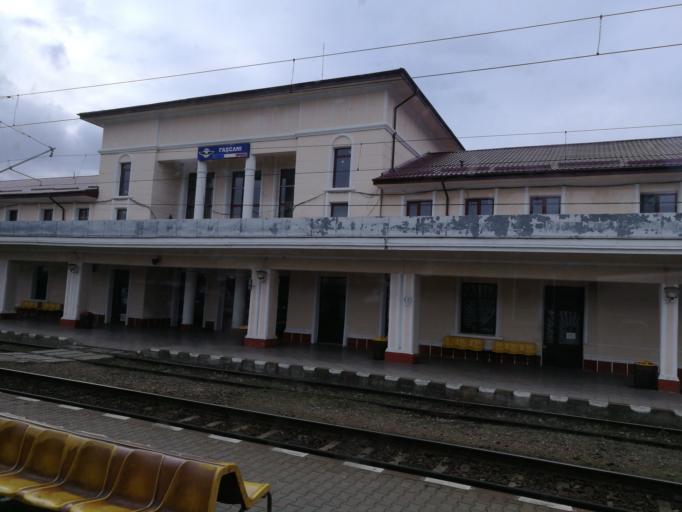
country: RO
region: Iasi
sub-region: Municipiul Pascani
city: Pascani
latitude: 47.2571
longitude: 26.7242
